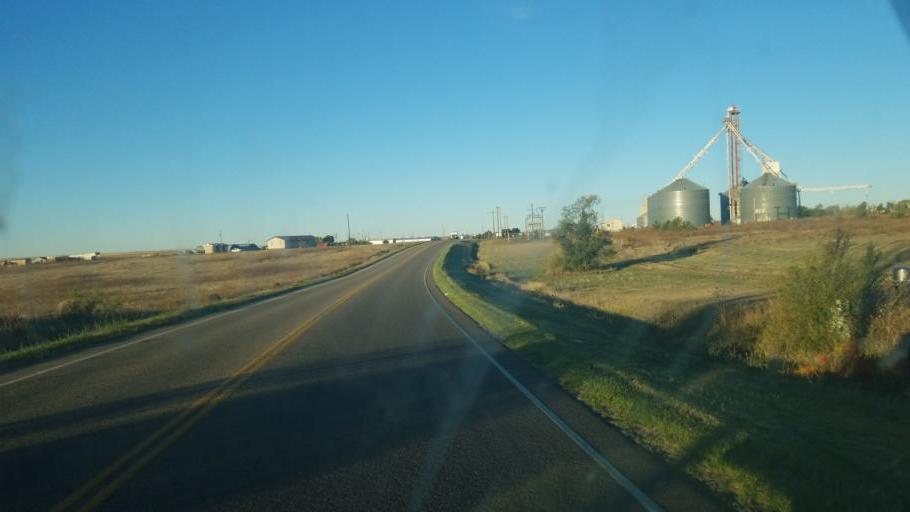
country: US
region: Colorado
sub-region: Cheyenne County
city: Cheyenne Wells
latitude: 38.8173
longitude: -102.3459
